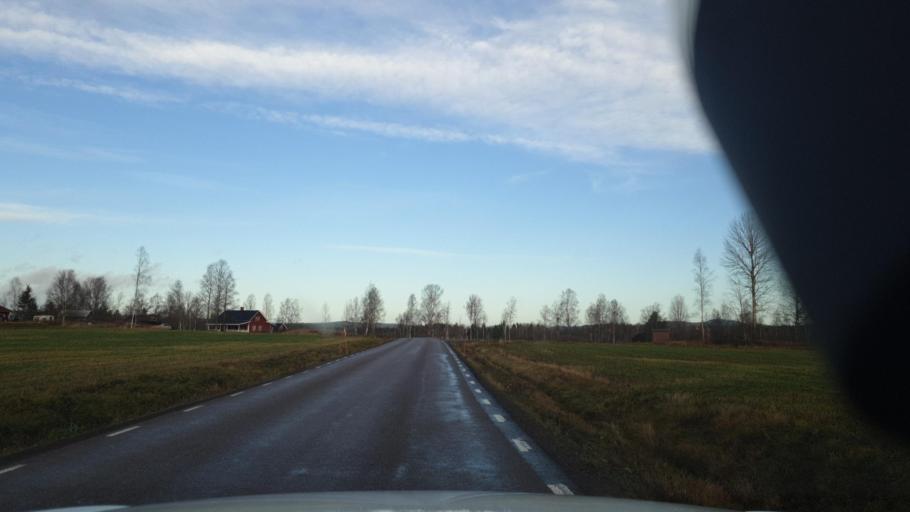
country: SE
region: Vaermland
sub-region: Eda Kommun
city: Charlottenberg
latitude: 59.7608
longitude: 12.2125
